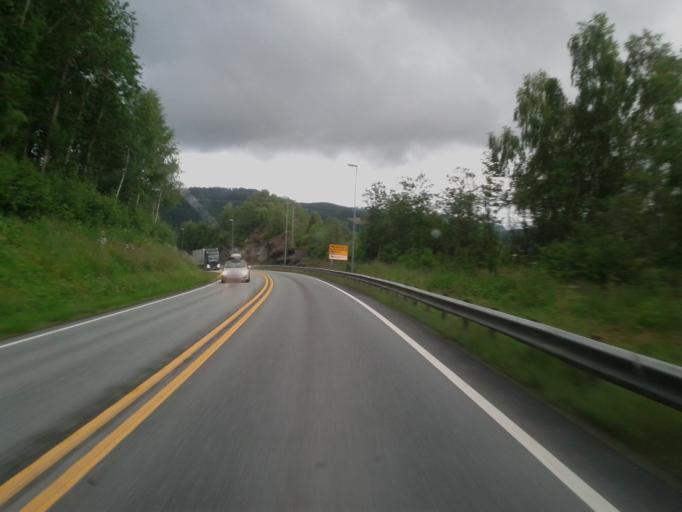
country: NO
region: Sor-Trondelag
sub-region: Melhus
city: Lundamo
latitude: 63.1117
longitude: 10.2356
